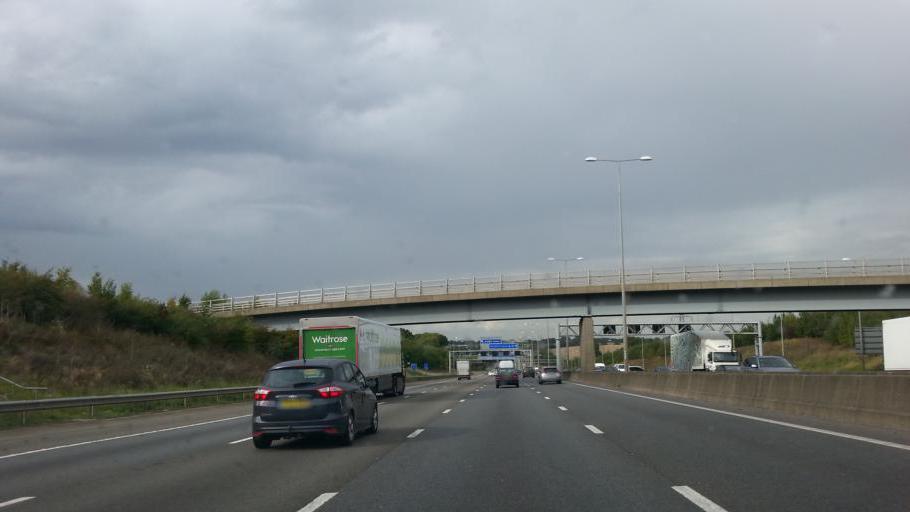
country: GB
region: England
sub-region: Hertfordshire
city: Flamstead
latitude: 51.8128
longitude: -0.4159
